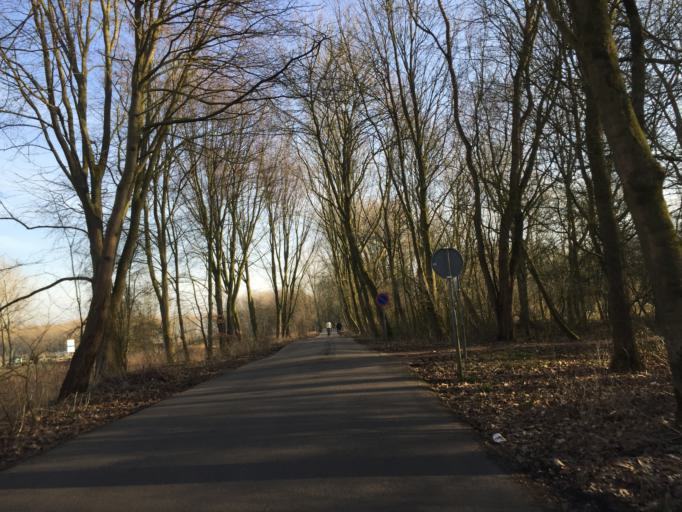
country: NL
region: South Holland
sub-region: Gemeente Den Haag
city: Ypenburg
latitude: 52.0234
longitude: 4.3863
